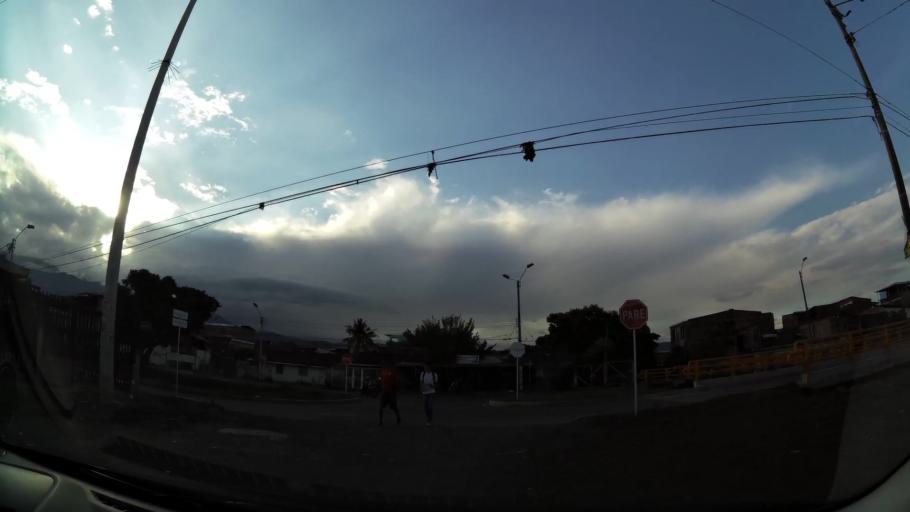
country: CO
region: Valle del Cauca
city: Cali
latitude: 3.4138
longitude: -76.5062
